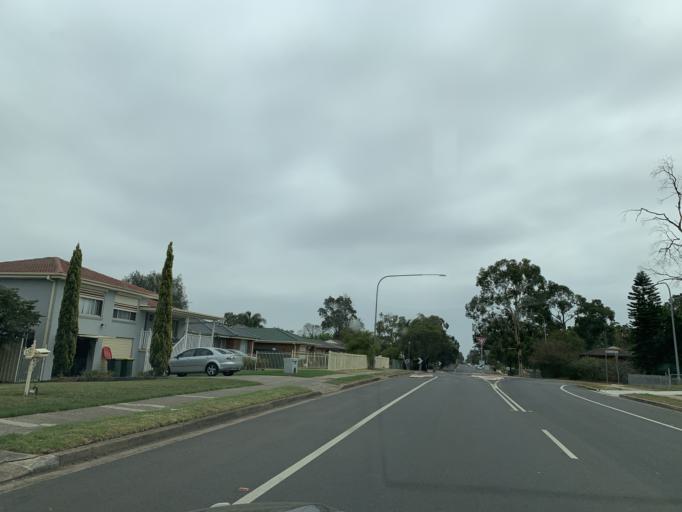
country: AU
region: New South Wales
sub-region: Blacktown
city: Doonside
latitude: -33.7527
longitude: 150.8714
